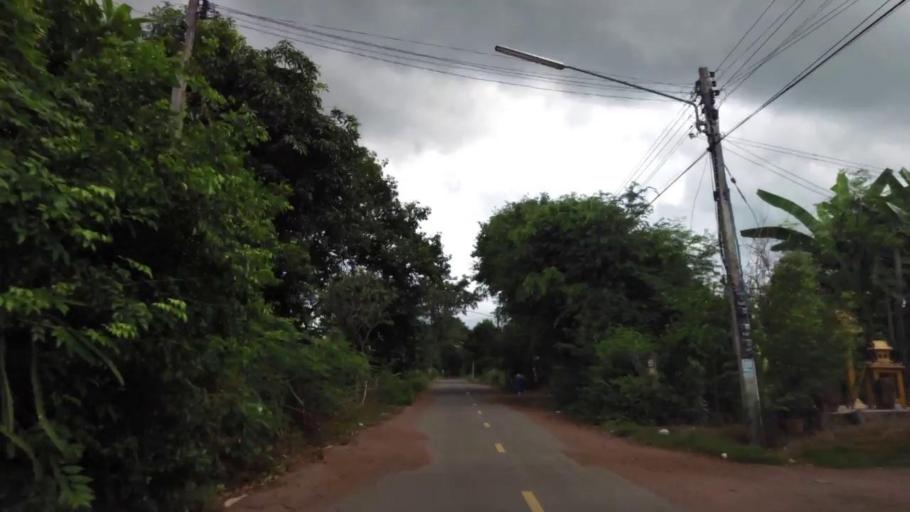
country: TH
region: Nakhon Sawan
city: Phai Sali
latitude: 15.6050
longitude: 100.6610
